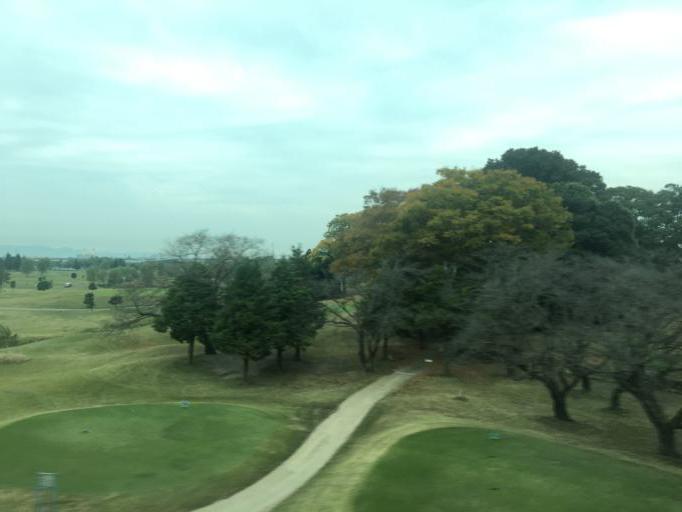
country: JP
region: Saitama
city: Kamifukuoka
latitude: 35.9097
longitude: 139.5531
